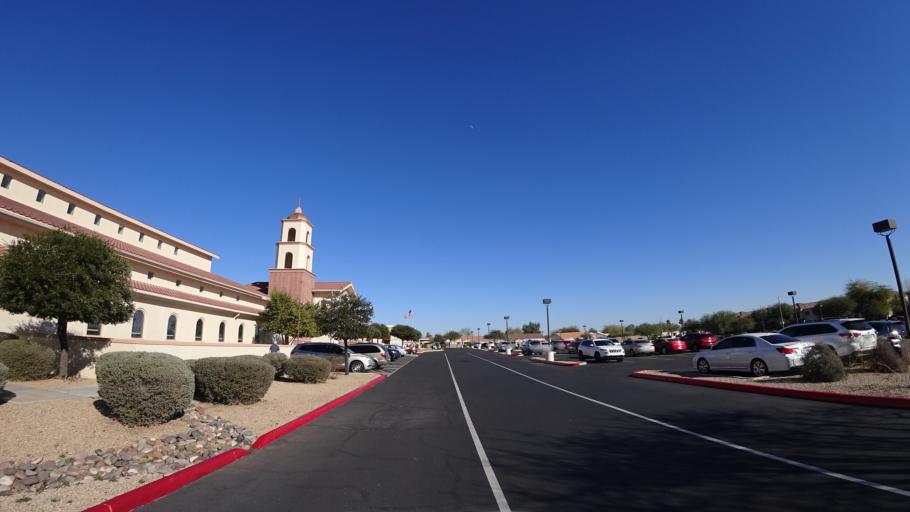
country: US
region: Arizona
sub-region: Maricopa County
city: Sun City West
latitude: 33.6877
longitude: -112.3814
